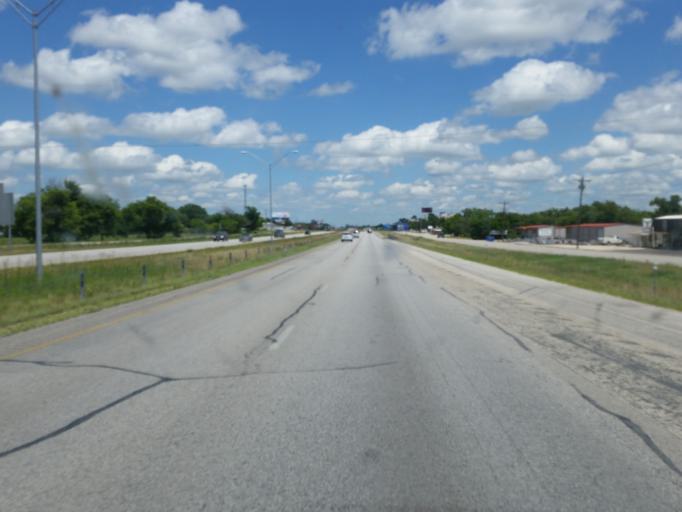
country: US
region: Texas
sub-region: Callahan County
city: Clyde
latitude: 32.4142
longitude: -99.5033
